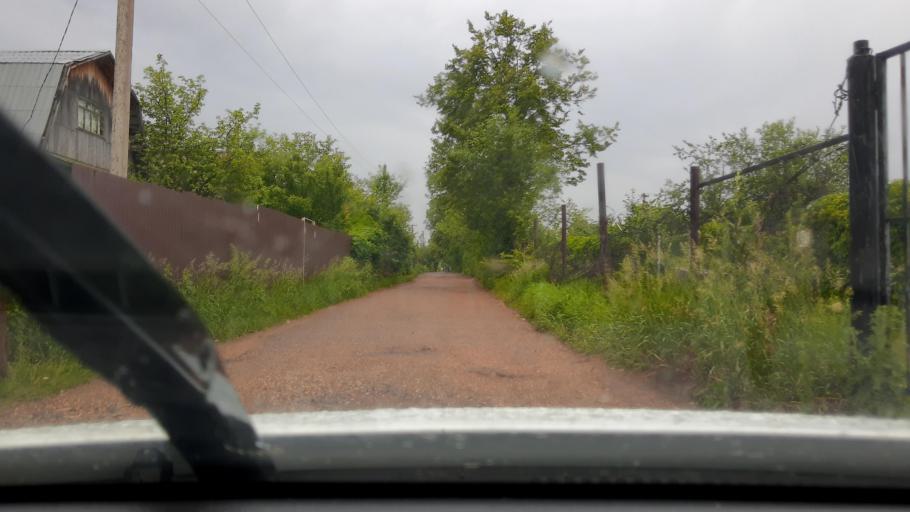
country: RU
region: Bashkortostan
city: Karmaskaly
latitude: 54.3802
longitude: 55.9123
